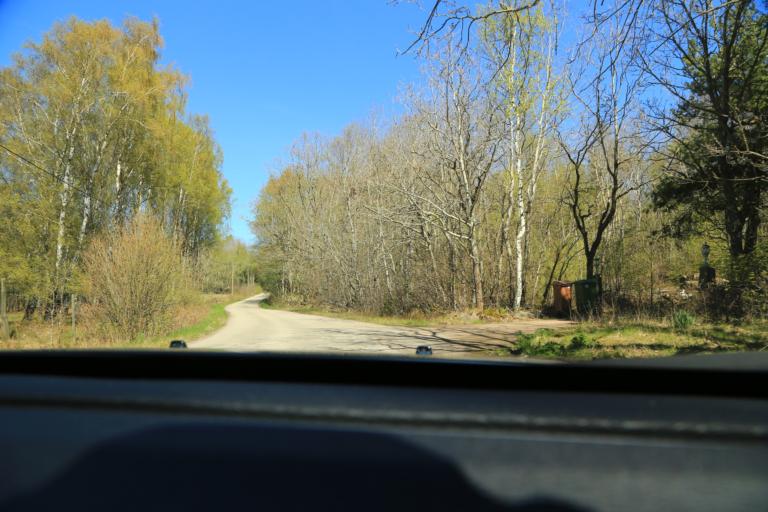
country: SE
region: Halland
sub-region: Varbergs Kommun
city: Traslovslage
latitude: 57.0916
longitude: 12.2883
